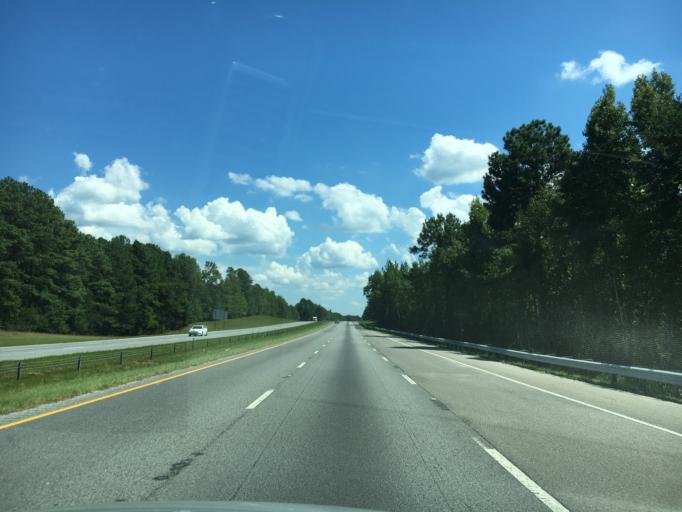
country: US
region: South Carolina
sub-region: Spartanburg County
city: Woodruff
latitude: 34.6612
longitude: -81.9258
